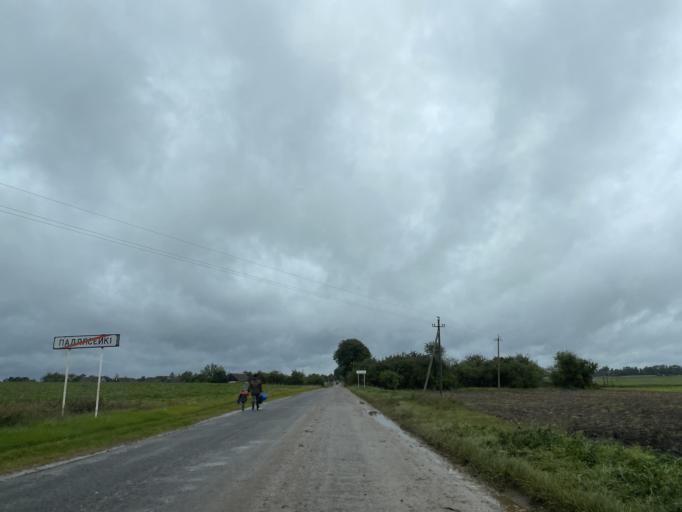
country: BY
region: Brest
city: Lyakhavichy
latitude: 53.1890
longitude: 26.2510
